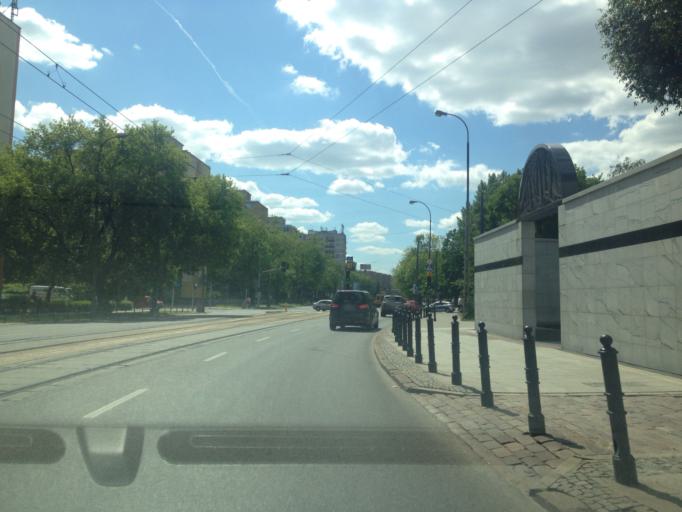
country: PL
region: Masovian Voivodeship
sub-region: Warszawa
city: Wola
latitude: 52.2523
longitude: 20.9893
